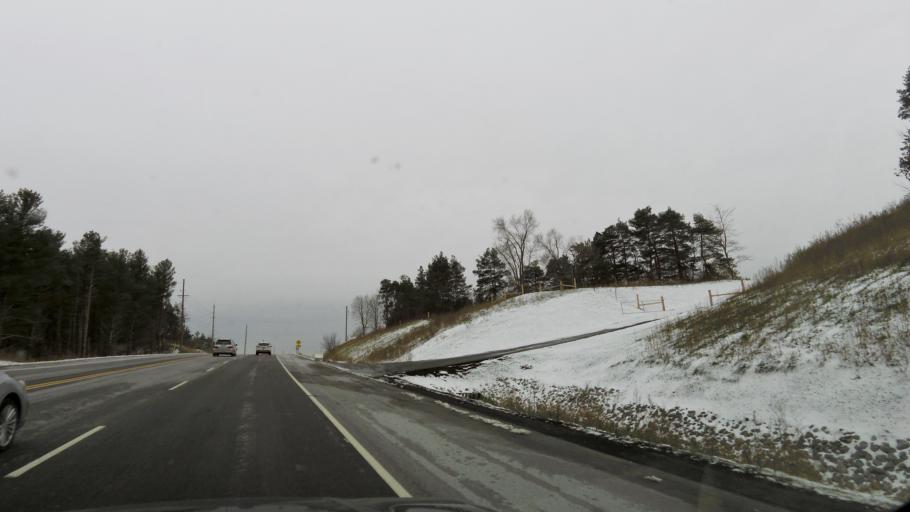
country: CA
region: Ontario
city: Newmarket
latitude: 44.0839
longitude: -79.5151
